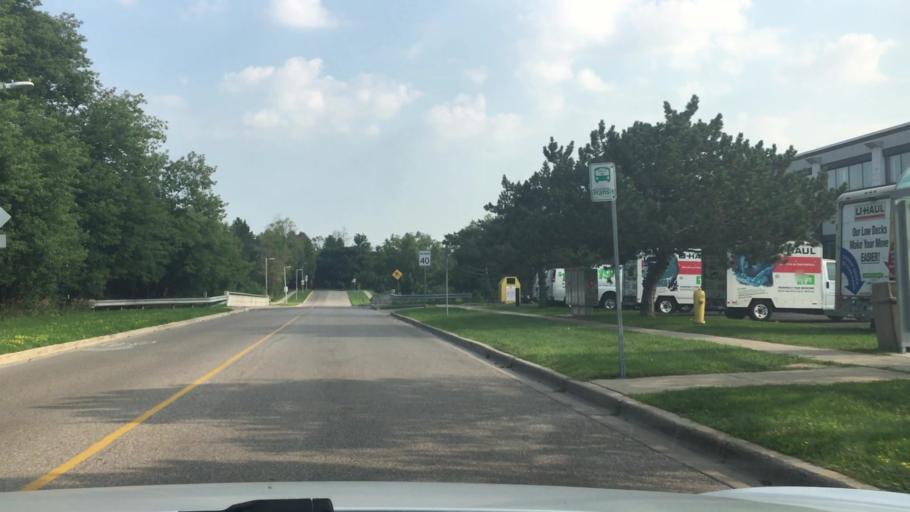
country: CA
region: Ontario
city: Ajax
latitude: 43.8746
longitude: -78.9615
